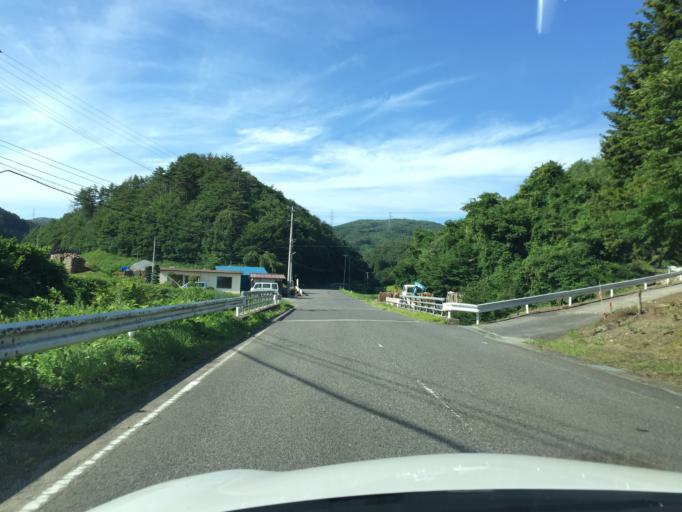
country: JP
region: Fukushima
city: Ishikawa
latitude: 37.2284
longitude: 140.4913
